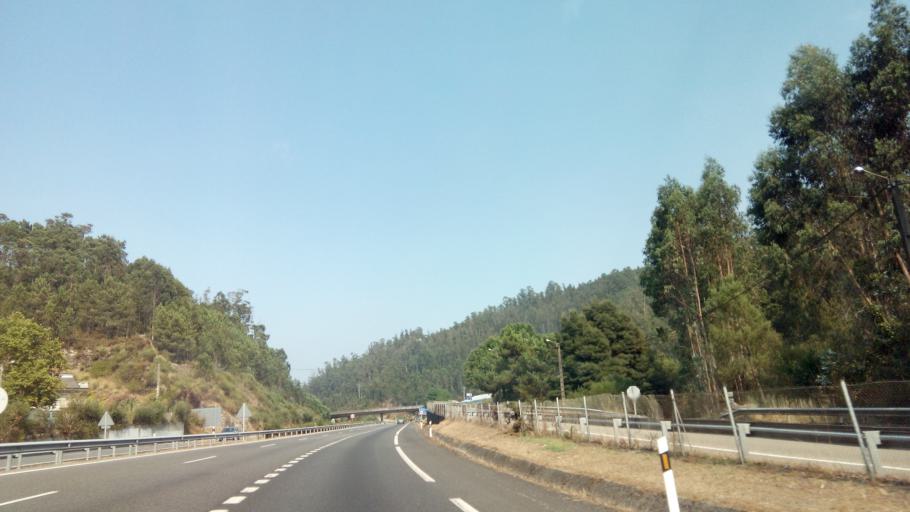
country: ES
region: Galicia
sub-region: Provincia de Pontevedra
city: Porrino
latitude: 42.1712
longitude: -8.5869
